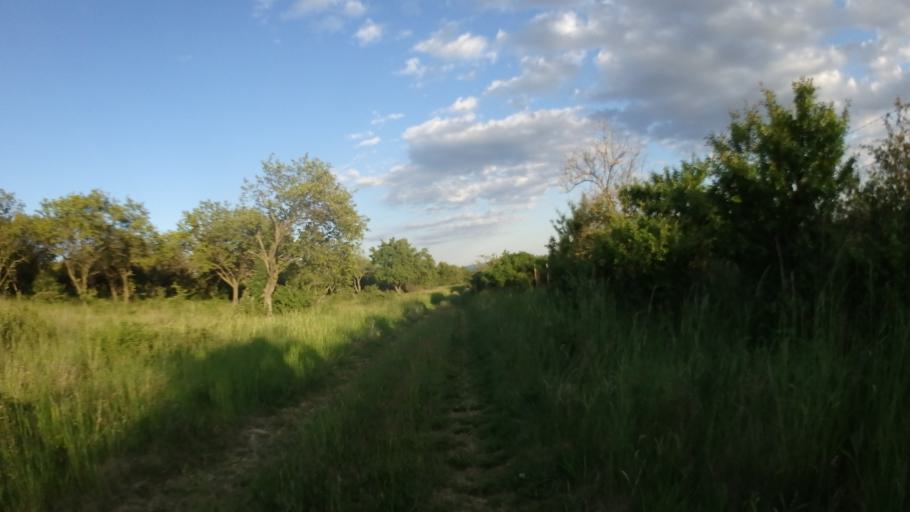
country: CZ
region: South Moravian
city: Zelesice
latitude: 49.1258
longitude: 16.5846
